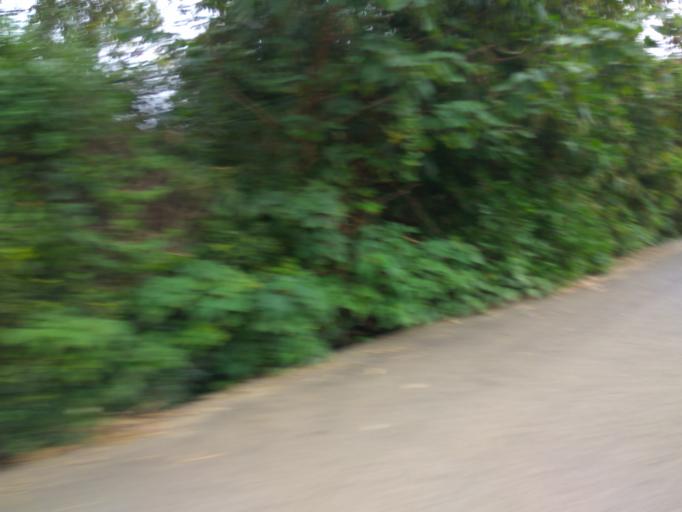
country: TW
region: Taiwan
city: Taoyuan City
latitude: 24.9946
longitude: 121.2241
